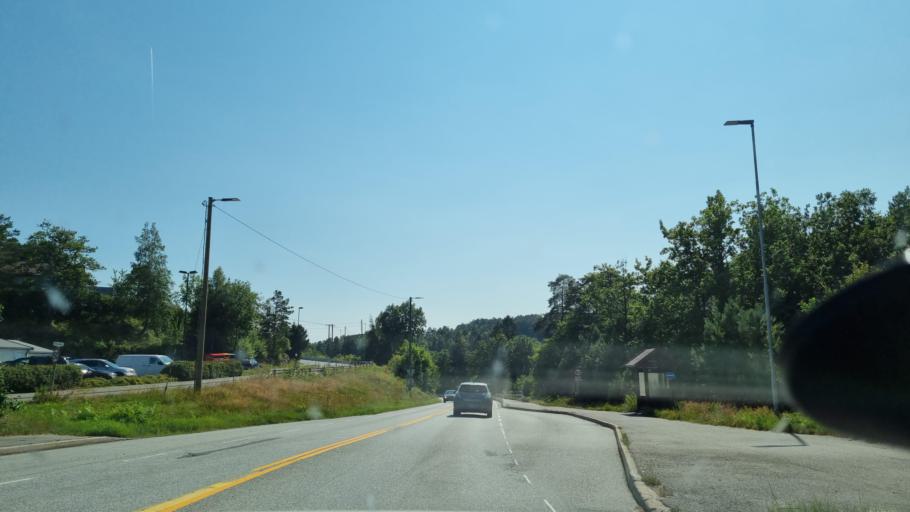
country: NO
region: Aust-Agder
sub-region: Arendal
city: Arendal
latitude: 58.4643
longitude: 8.8214
